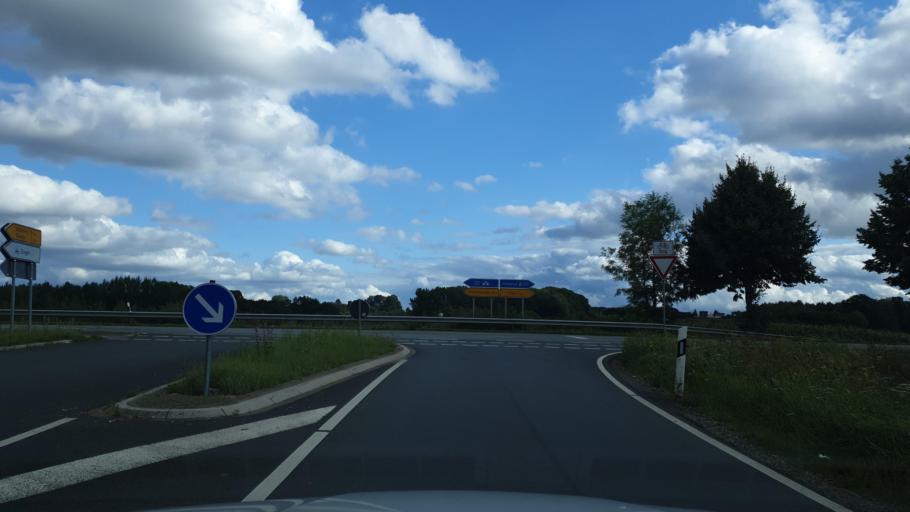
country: DE
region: North Rhine-Westphalia
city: Enger
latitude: 52.1455
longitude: 8.5751
